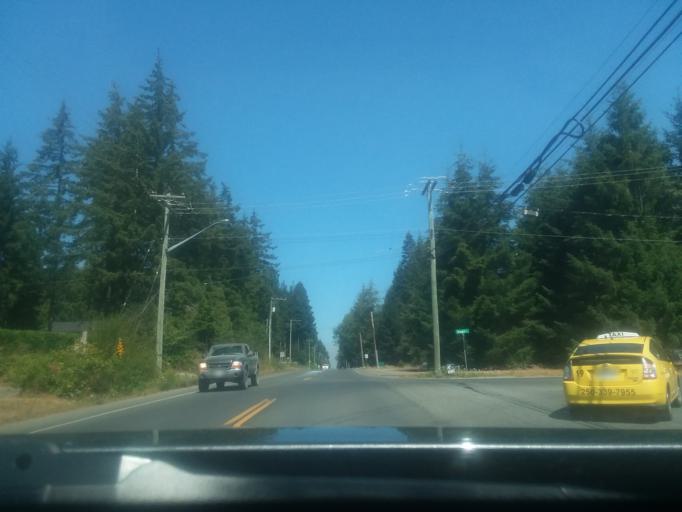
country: CA
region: British Columbia
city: Courtenay
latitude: 49.7008
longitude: -124.9343
